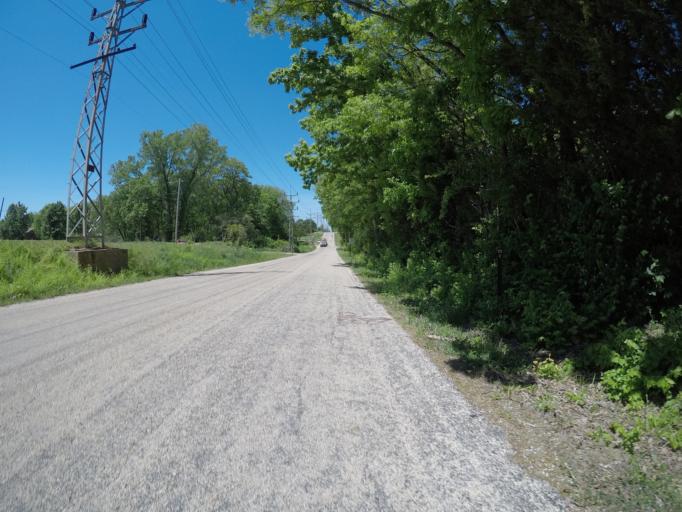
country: US
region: Kansas
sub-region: Shawnee County
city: Topeka
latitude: 39.0518
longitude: -95.5909
